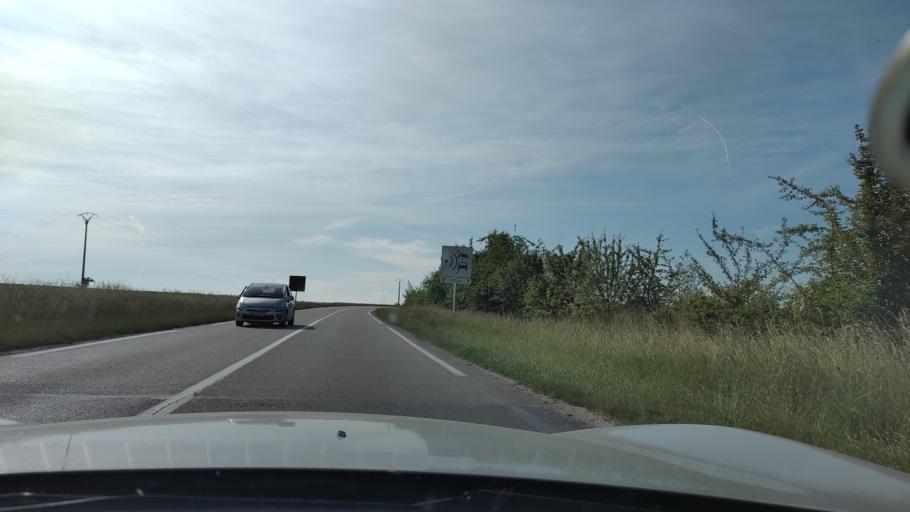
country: FR
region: Ile-de-France
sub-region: Departement de Seine-et-Marne
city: Jouy-le-Chatel
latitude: 48.6685
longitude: 3.1334
